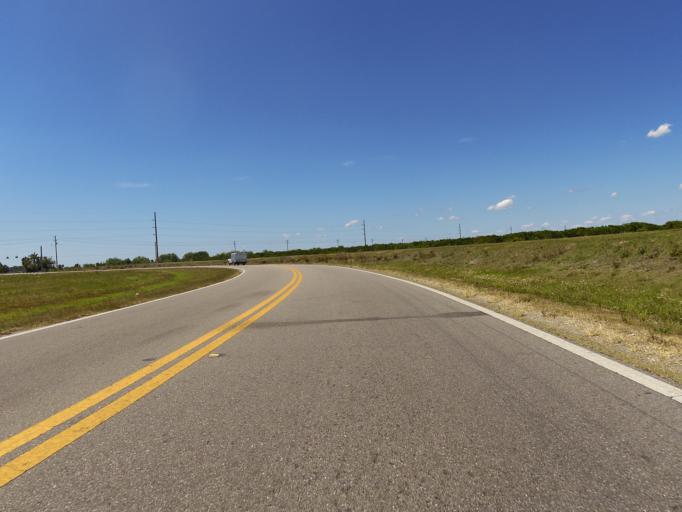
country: US
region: Florida
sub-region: Collier County
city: Immokalee
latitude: 26.3745
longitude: -81.4147
